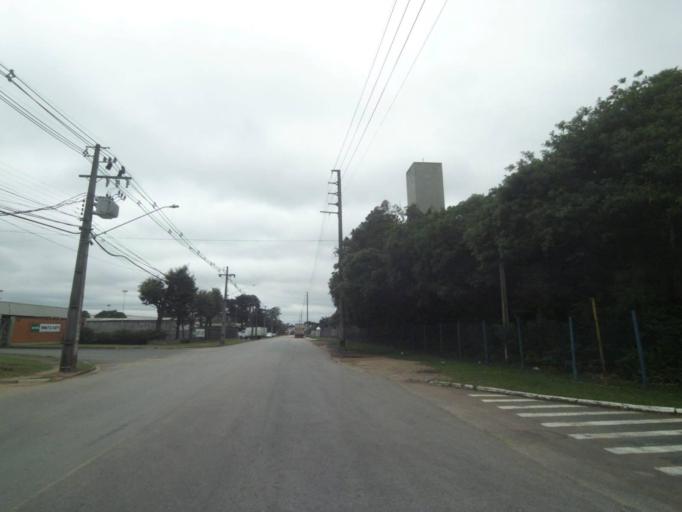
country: BR
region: Parana
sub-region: Sao Jose Dos Pinhais
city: Sao Jose dos Pinhais
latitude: -25.5556
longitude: -49.3086
